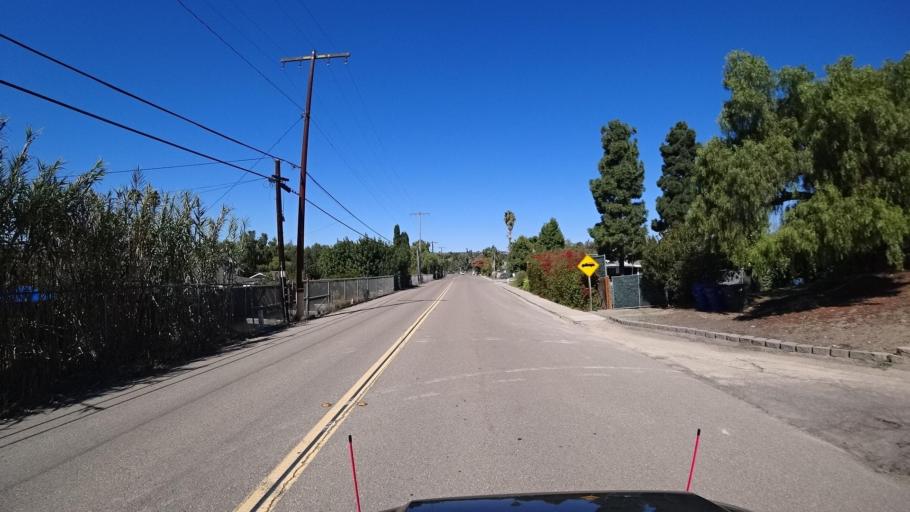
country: US
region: California
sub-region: San Diego County
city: Bonita
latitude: 32.6638
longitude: -117.0231
